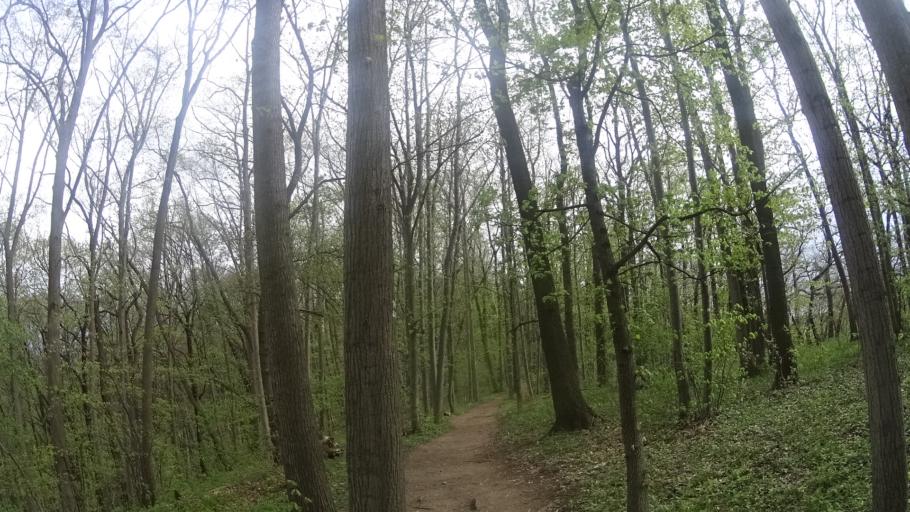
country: DE
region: Thuringia
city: Wandersleben
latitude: 50.8588
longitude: 10.8592
